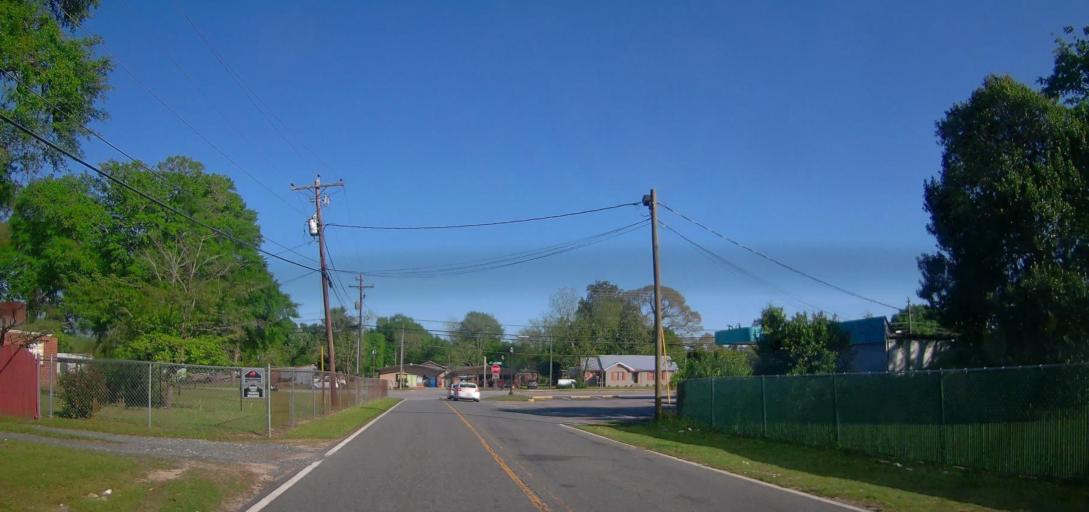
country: US
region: Georgia
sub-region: Houston County
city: Perry
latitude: 32.4511
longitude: -83.7459
